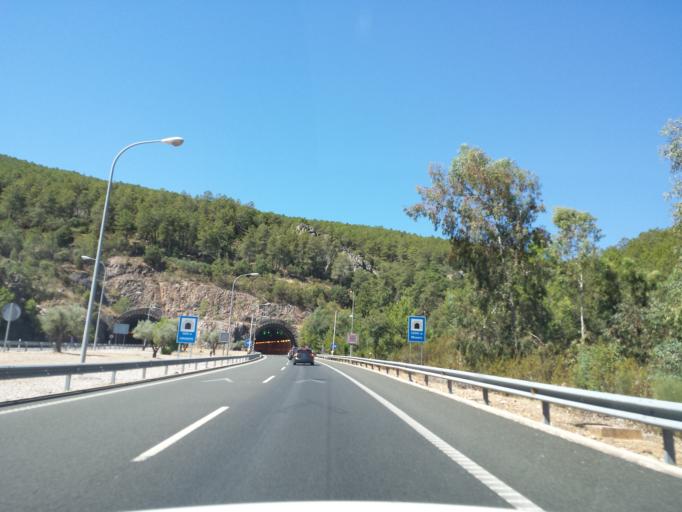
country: ES
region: Extremadura
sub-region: Provincia de Caceres
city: Higuera
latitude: 39.6975
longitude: -5.6952
